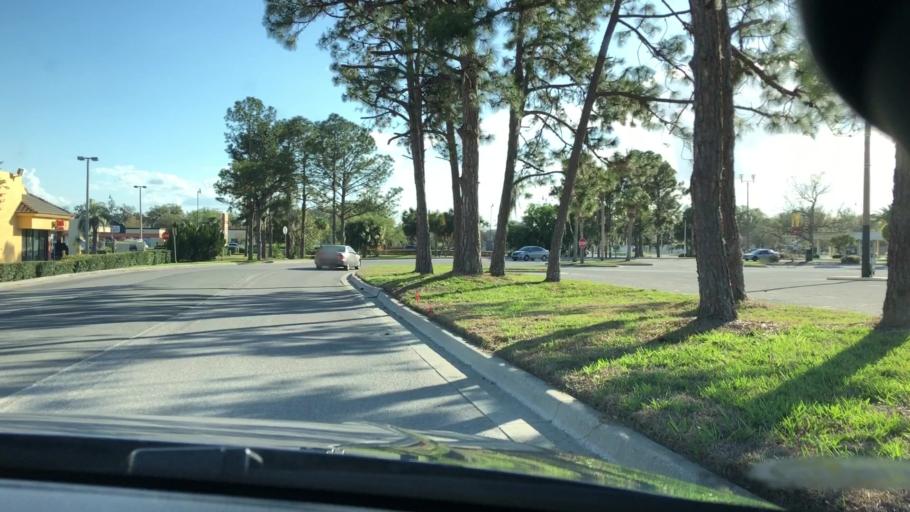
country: US
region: Florida
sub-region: Lake County
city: Silver Lake
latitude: 28.8236
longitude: -81.7825
